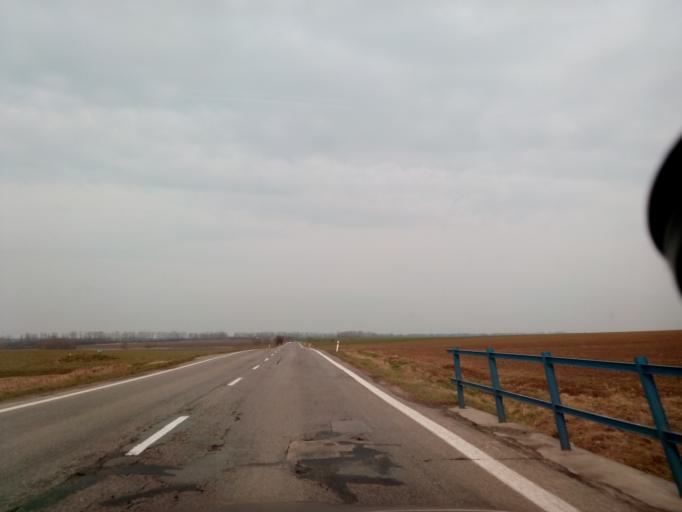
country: SK
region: Kosicky
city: Trebisov
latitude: 48.5314
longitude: 21.6735
